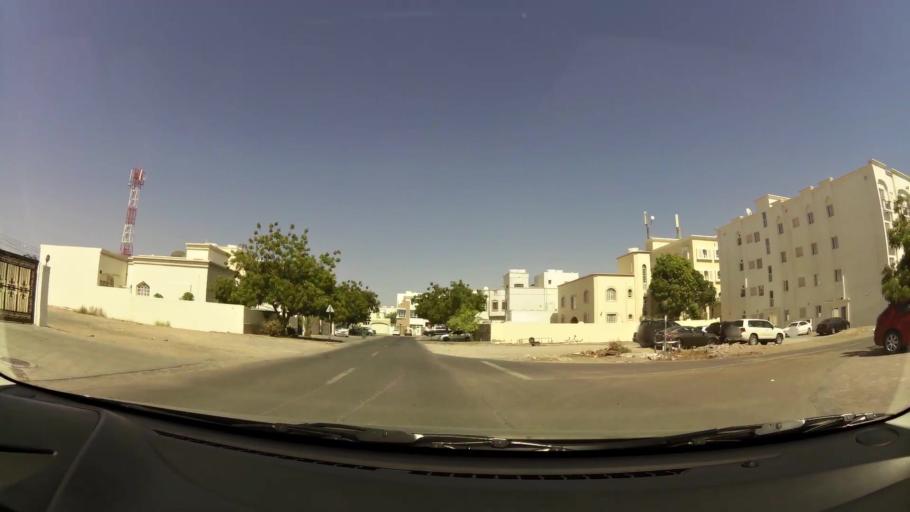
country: OM
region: Muhafazat Masqat
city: As Sib al Jadidah
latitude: 23.5946
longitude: 58.2477
